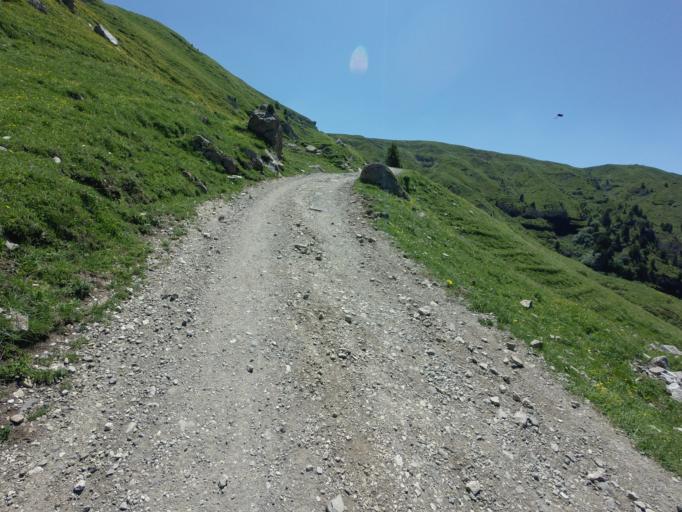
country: IT
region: Trentino-Alto Adige
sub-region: Provincia di Trento
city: Mazzin
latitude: 46.5085
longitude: 11.6961
